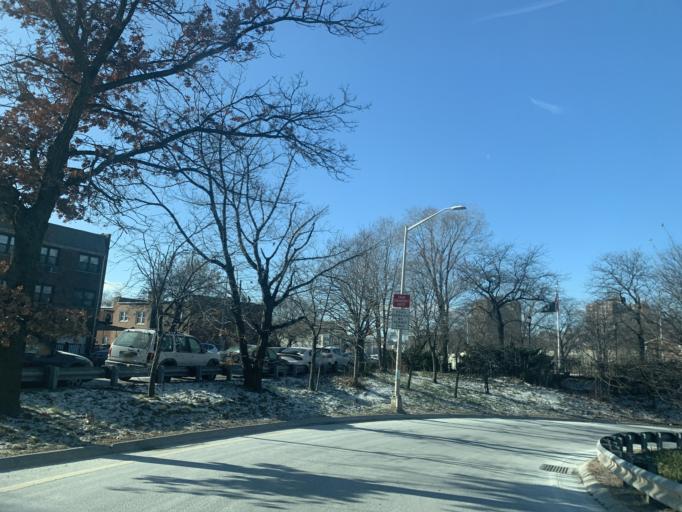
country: US
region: New York
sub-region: Queens County
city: Long Island City
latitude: 40.7399
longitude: -73.8988
